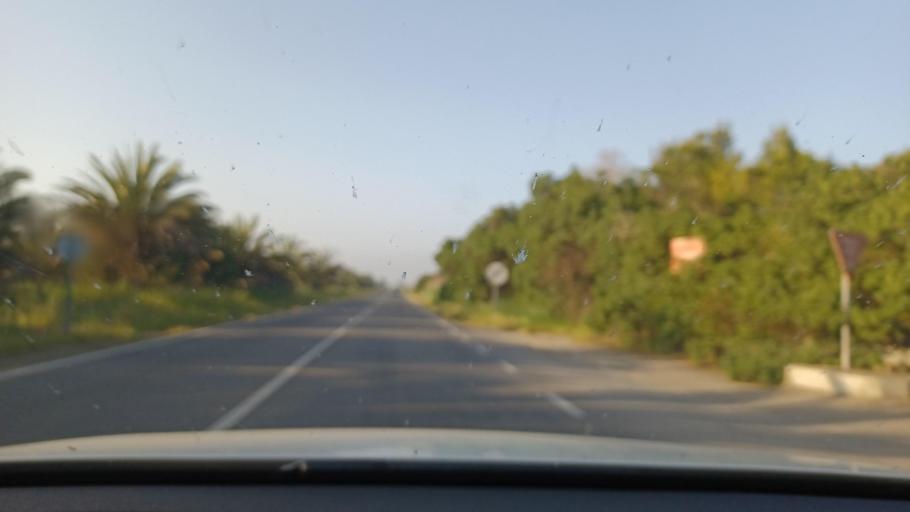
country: ES
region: Valencia
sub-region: Provincia de Alicante
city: Dolores
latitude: 38.1771
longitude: -0.7020
